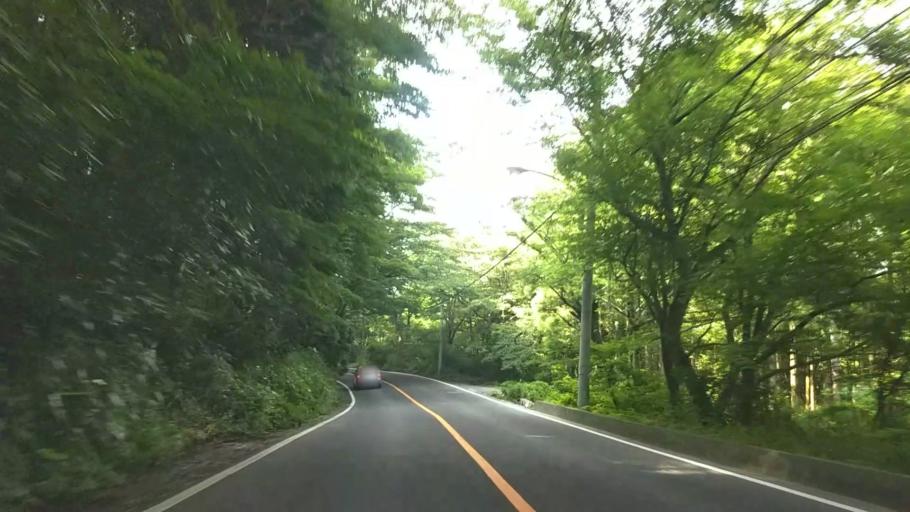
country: JP
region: Kanagawa
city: Hakone
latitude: 35.2270
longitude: 139.0494
